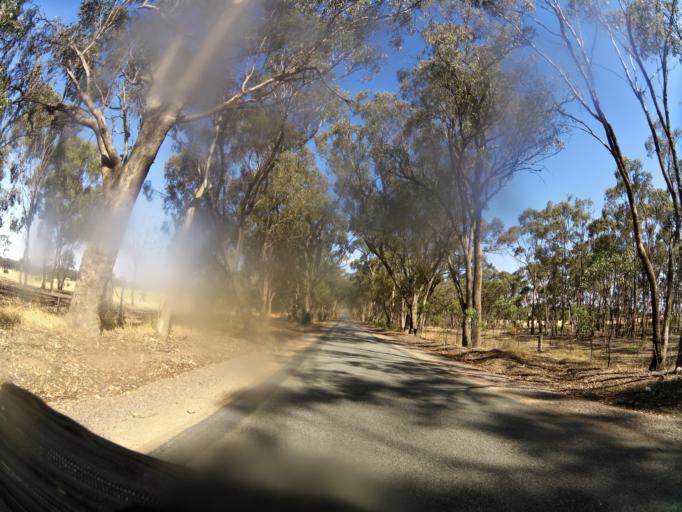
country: AU
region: Victoria
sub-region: Campaspe
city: Kyabram
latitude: -36.8796
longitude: 145.0895
